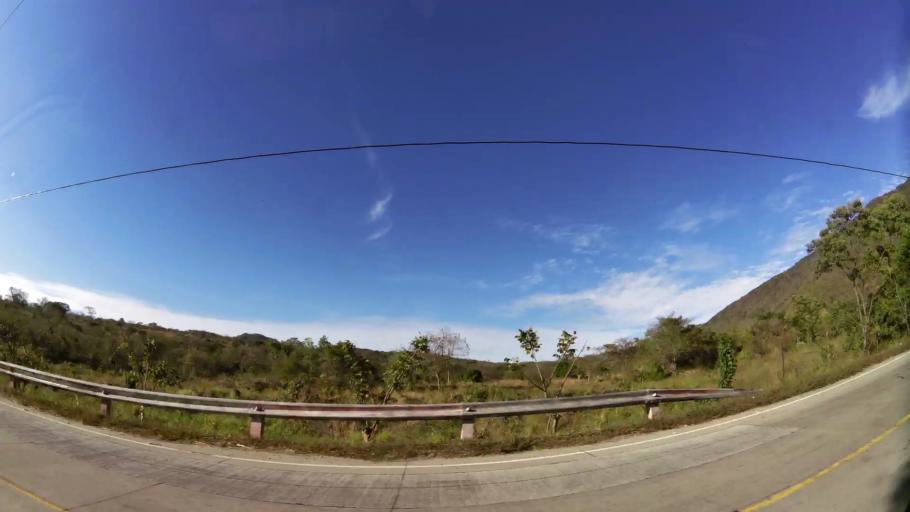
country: SV
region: Santa Ana
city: Metapan
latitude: 14.2513
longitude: -89.4640
